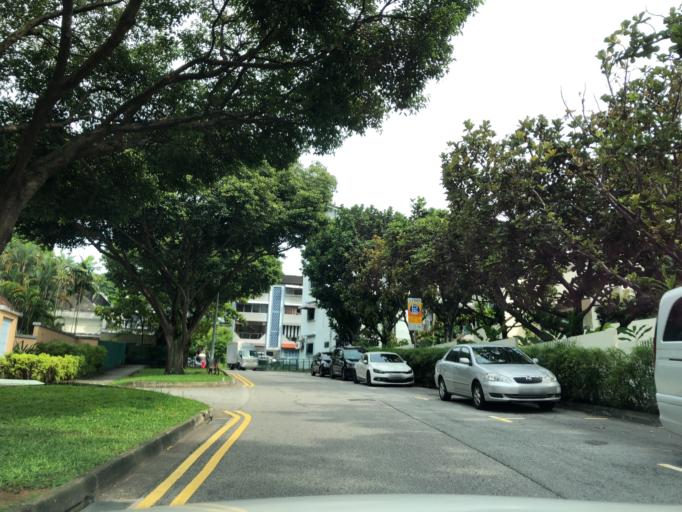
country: SG
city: Singapore
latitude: 1.2971
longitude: 103.8397
